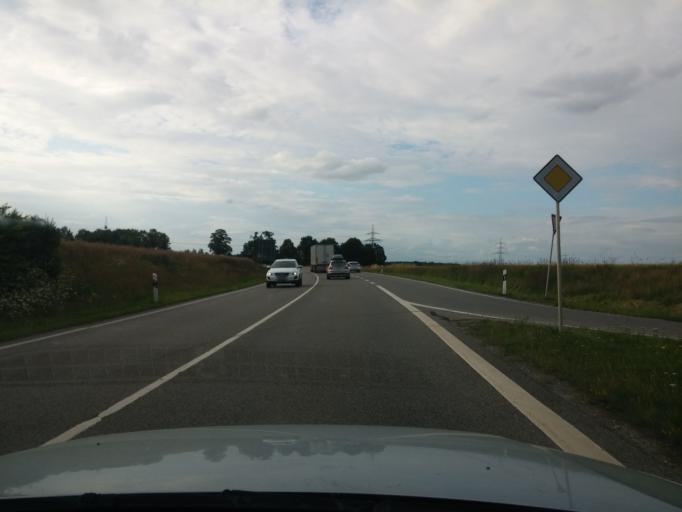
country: DE
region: Bavaria
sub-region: Upper Bavaria
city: Zorneding
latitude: 48.0816
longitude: 11.8098
